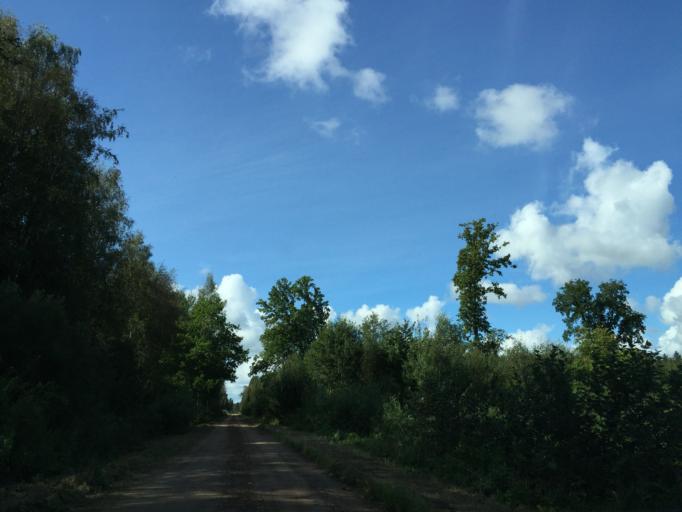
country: LV
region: Kuldigas Rajons
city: Kuldiga
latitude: 56.9921
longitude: 21.8404
